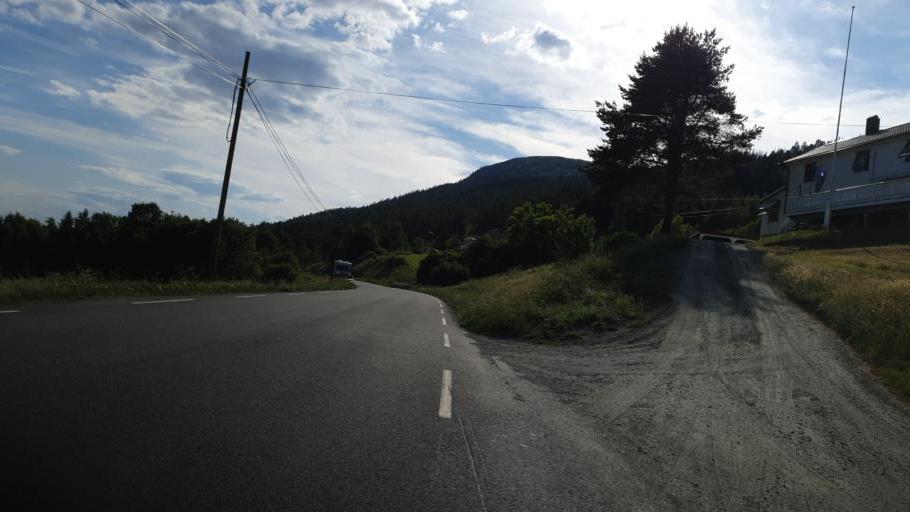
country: NO
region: Sor-Trondelag
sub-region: Trondheim
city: Trondheim
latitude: 63.5741
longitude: 10.3535
